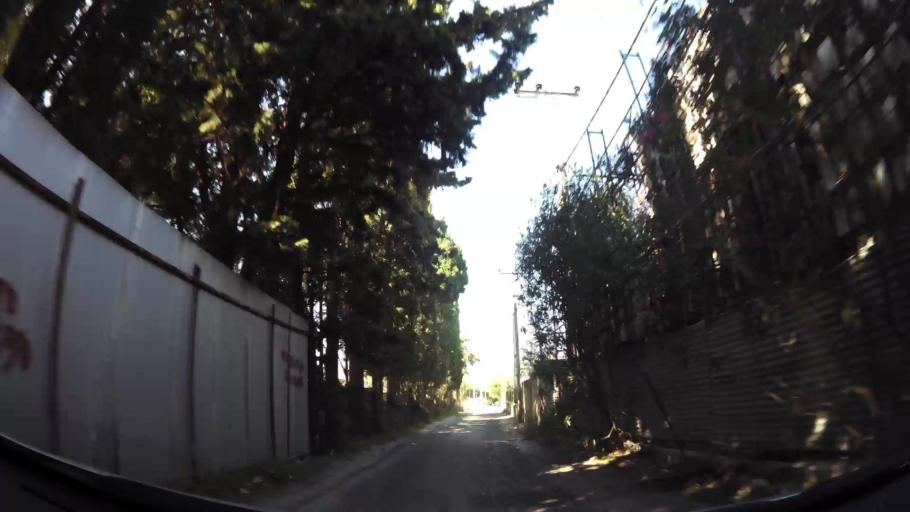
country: GR
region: Attica
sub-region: Nomarchia Athinas
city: Lykovrysi
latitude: 38.0869
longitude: 23.7815
